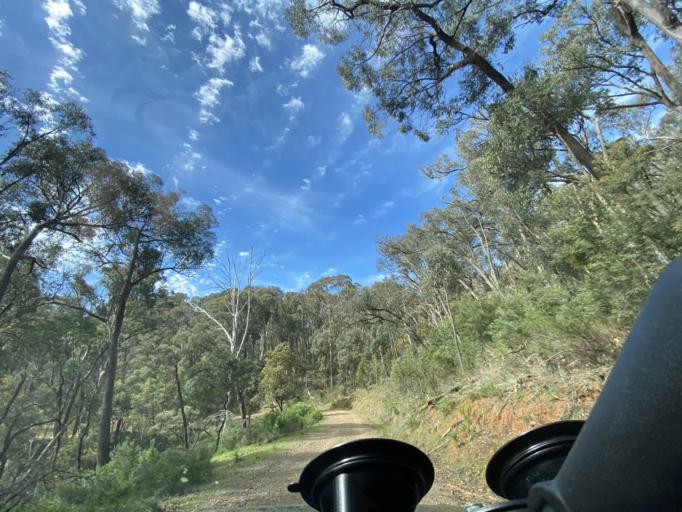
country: AU
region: Victoria
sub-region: Mansfield
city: Mansfield
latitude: -36.8159
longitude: 146.1025
